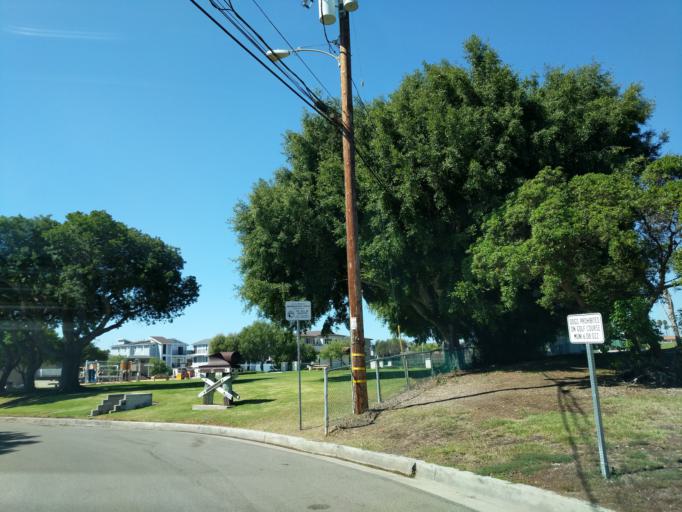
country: US
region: California
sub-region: Orange County
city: San Clemente
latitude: 33.4058
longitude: -117.5959
